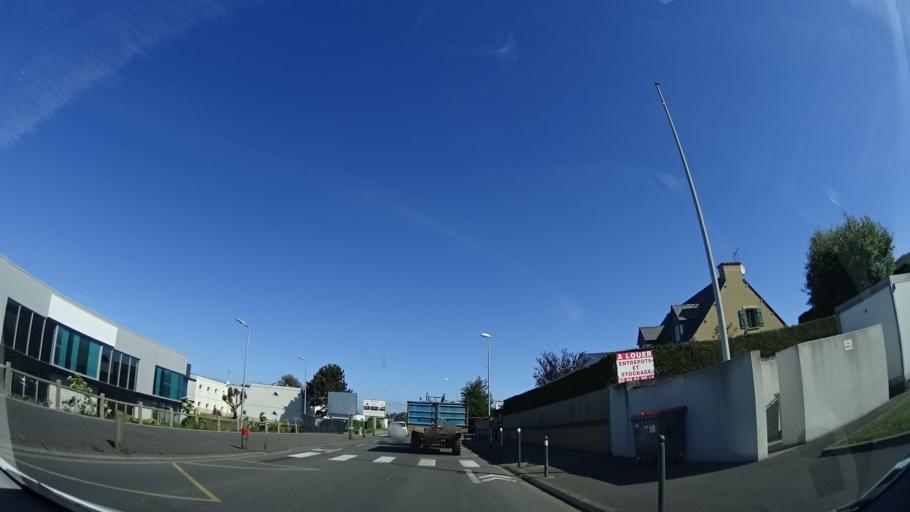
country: FR
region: Brittany
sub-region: Departement d'Ille-et-Vilaine
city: Saint-Jouan-des-Guerets
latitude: 48.6209
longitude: -1.9864
